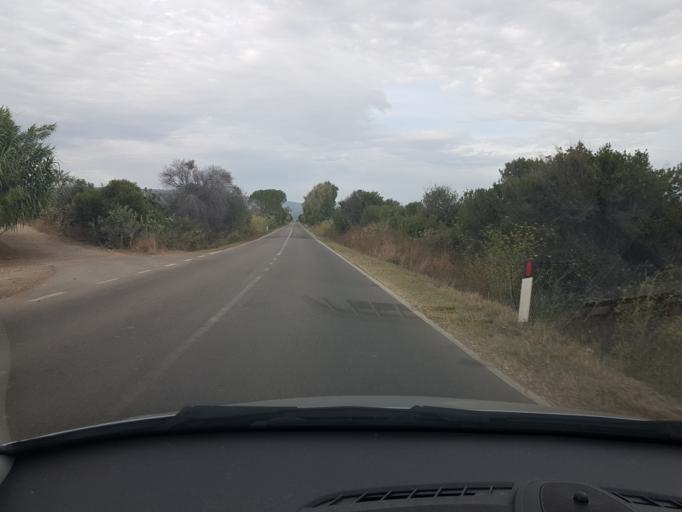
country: IT
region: Sardinia
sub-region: Provincia di Oristano
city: Riola Sardo
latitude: 40.0049
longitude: 8.5380
